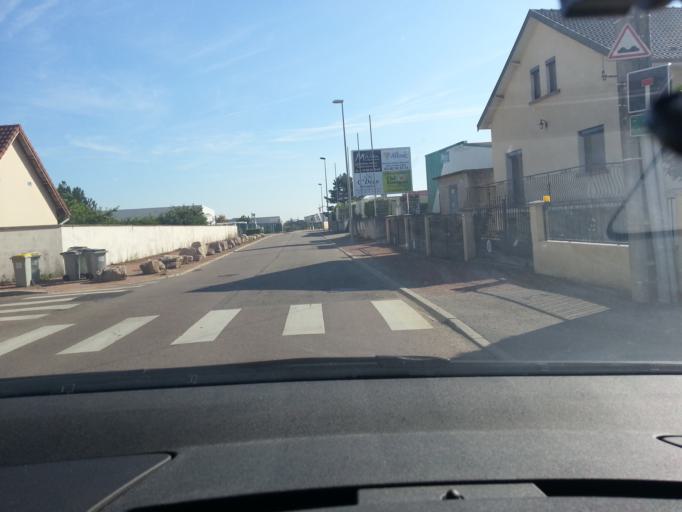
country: FR
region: Bourgogne
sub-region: Departement de la Cote-d'Or
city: Perrigny-les-Dijon
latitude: 47.2773
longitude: 5.0135
